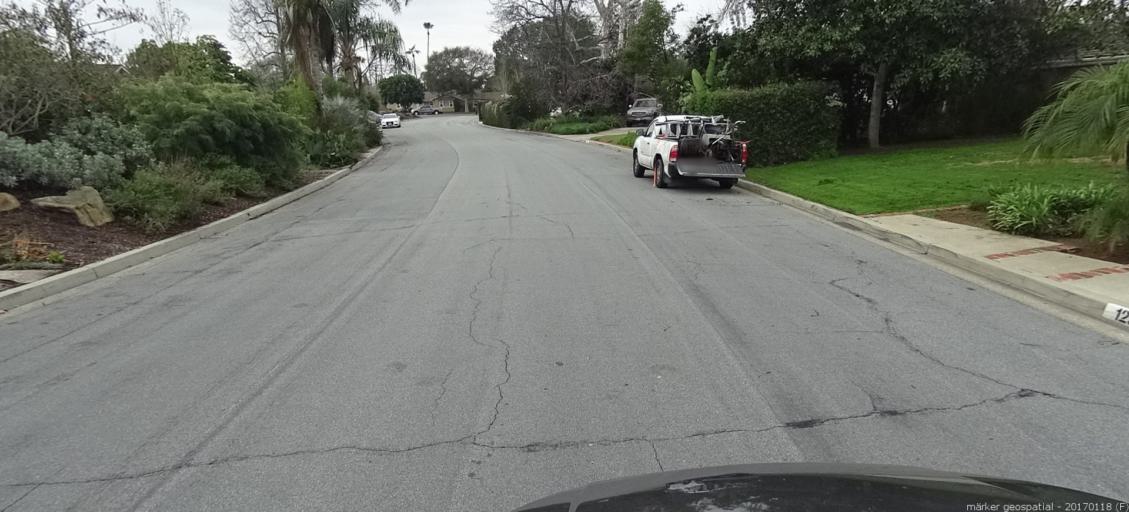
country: US
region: California
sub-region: Orange County
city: North Tustin
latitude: 33.7485
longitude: -117.7965
